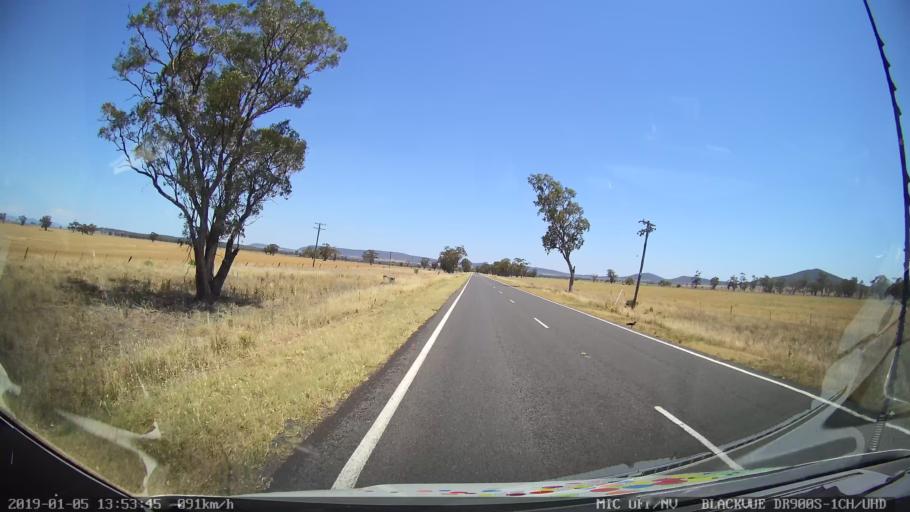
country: AU
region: New South Wales
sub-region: Gunnedah
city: Gunnedah
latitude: -31.0792
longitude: 150.2764
